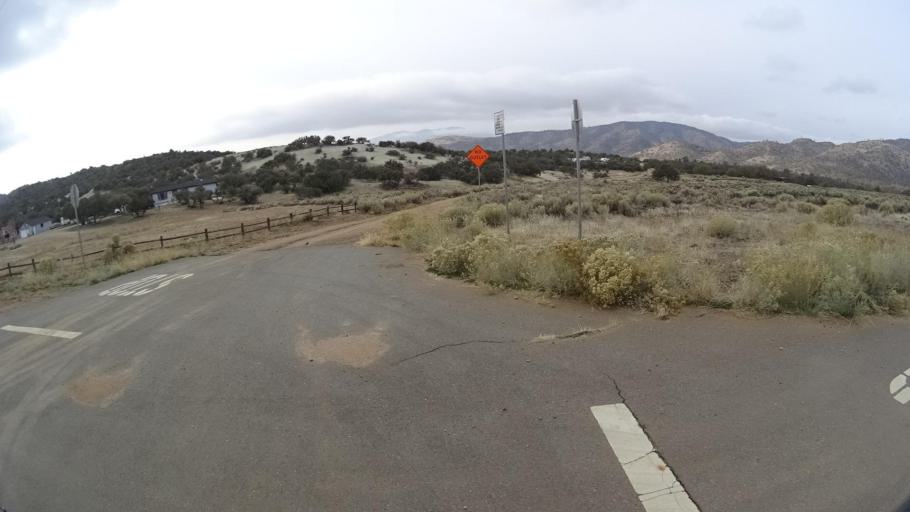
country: US
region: California
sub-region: Kern County
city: Tehachapi
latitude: 35.1777
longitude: -118.3717
